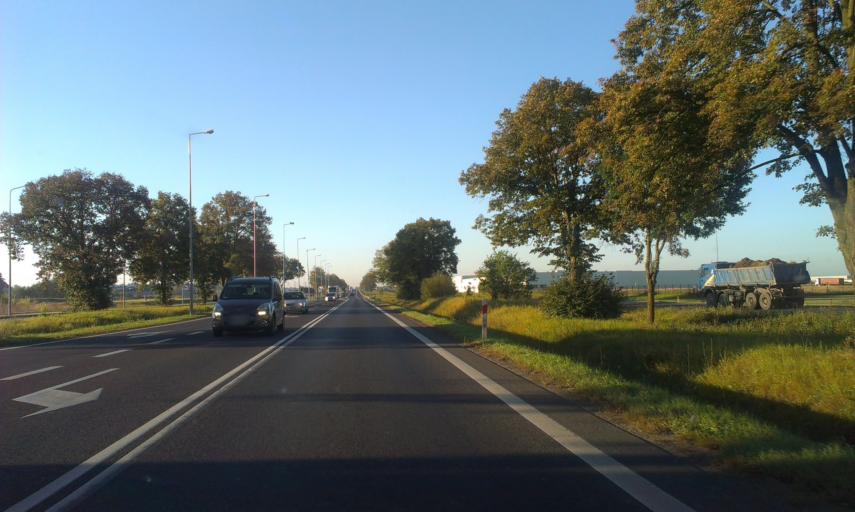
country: PL
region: Kujawsko-Pomorskie
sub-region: Powiat torunski
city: Lysomice
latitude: 53.1108
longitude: 18.6246
